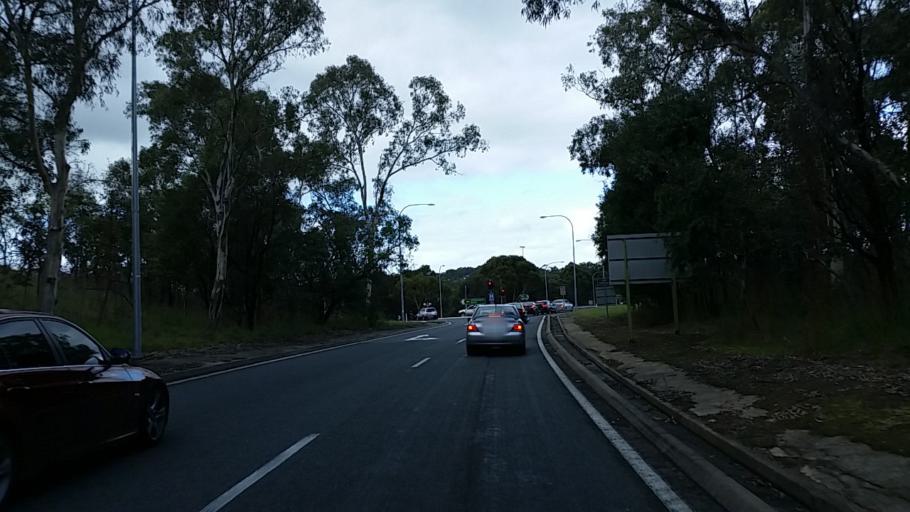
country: AU
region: South Australia
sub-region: Mount Barker
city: Little Hampton
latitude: -35.0576
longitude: 138.8511
